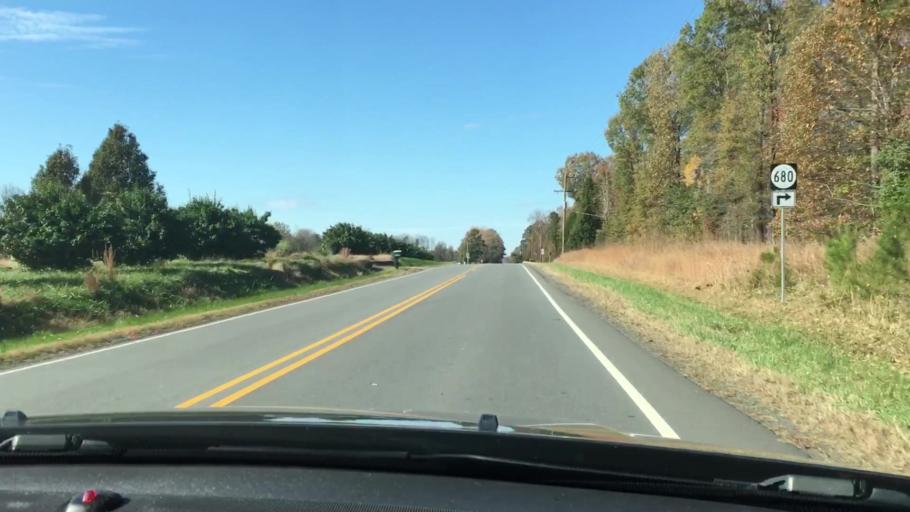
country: US
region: Virginia
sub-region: King William County
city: King William
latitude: 37.6977
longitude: -77.0381
